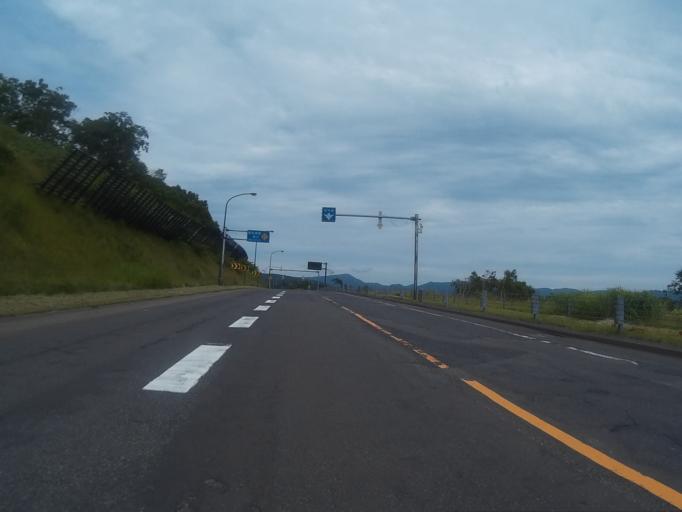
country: JP
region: Hokkaido
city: Sapporo
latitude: 42.8570
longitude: 141.0977
